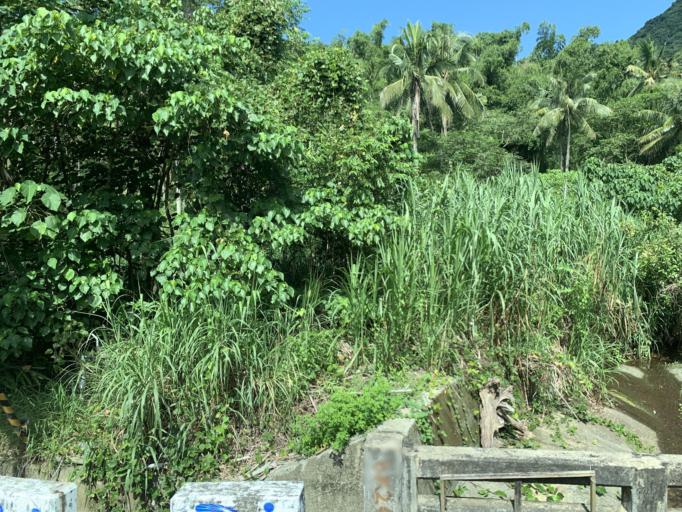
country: TW
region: Taiwan
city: Yujing
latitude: 22.9014
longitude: 120.5167
